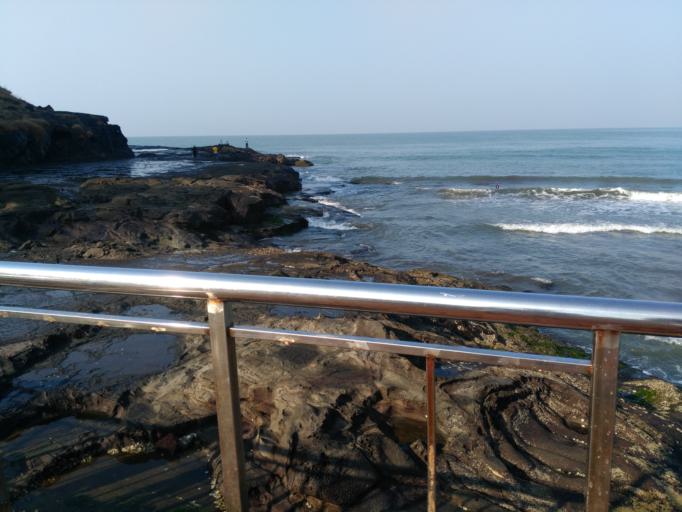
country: IN
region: Maharashtra
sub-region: Raigarh
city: Srivardhan
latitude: 17.9927
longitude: 73.0192
